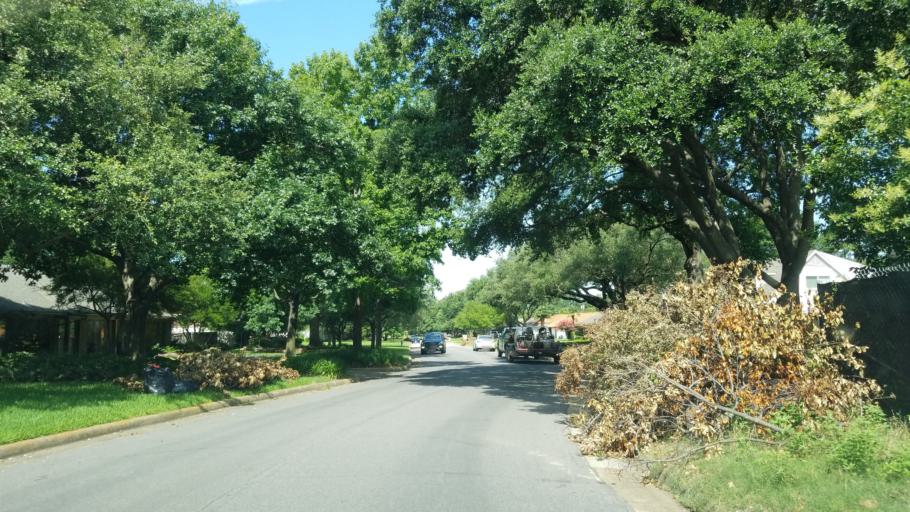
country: US
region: Texas
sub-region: Dallas County
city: Addison
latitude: 32.9059
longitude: -96.8400
